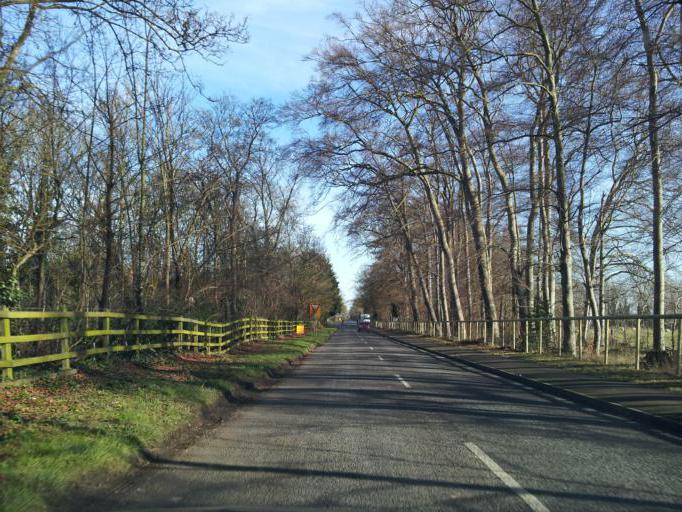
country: GB
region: England
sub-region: Cambridgeshire
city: Meldreth
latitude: 52.1092
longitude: 0.0404
